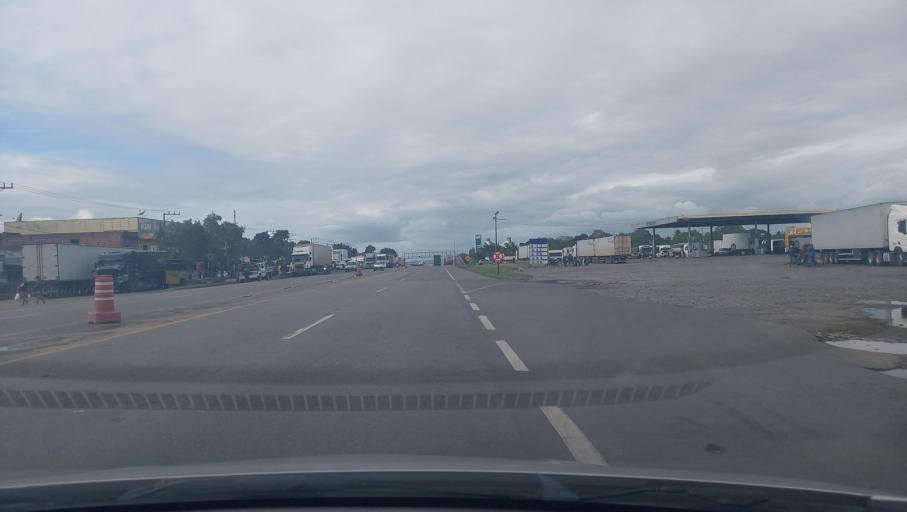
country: BR
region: Bahia
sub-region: Santo Estevao
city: Santo Estevao
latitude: -12.4408
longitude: -39.2296
